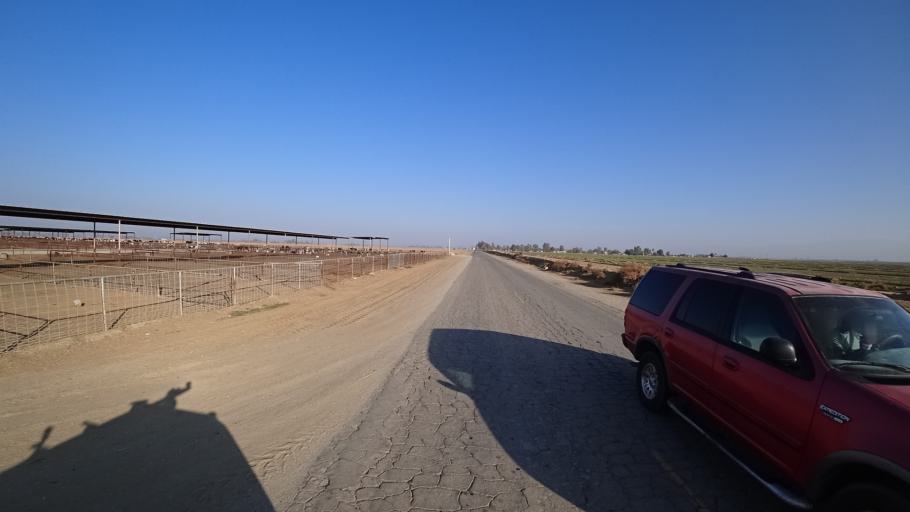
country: US
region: California
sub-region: Kern County
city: Greenfield
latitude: 35.2314
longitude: -118.9677
